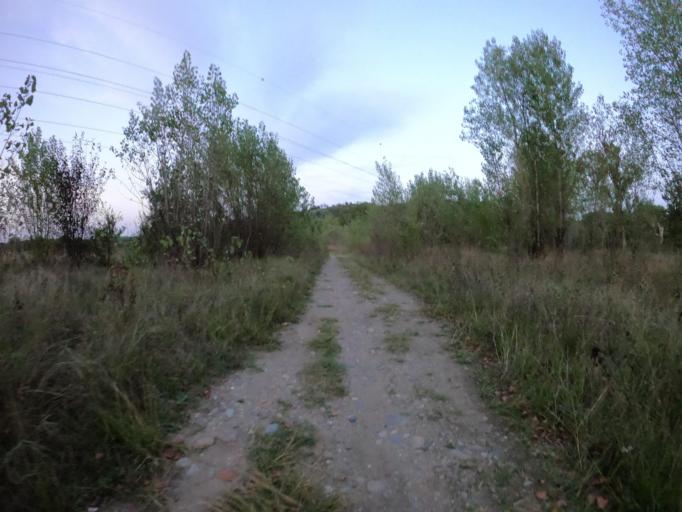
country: FR
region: Midi-Pyrenees
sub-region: Departement de la Haute-Garonne
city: Portet-sur-Garonne
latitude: 43.5291
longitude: 1.4233
